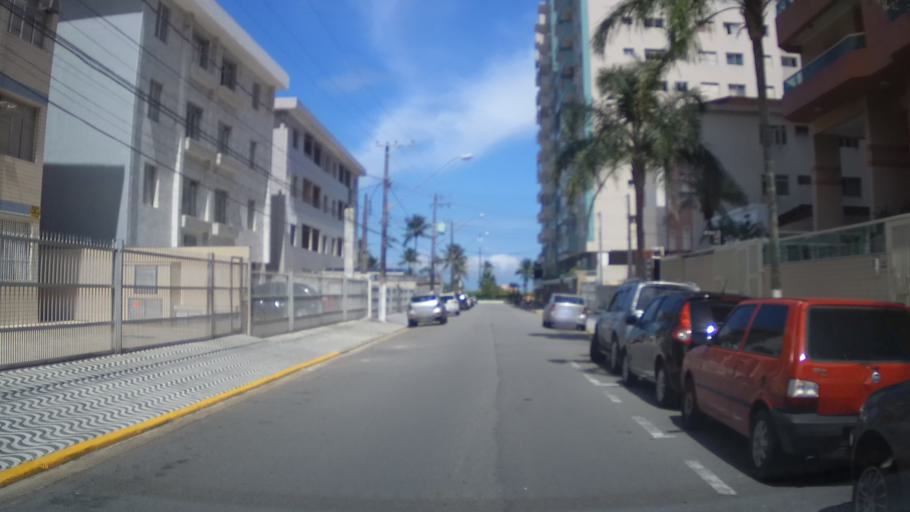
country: BR
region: Sao Paulo
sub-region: Praia Grande
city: Praia Grande
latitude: -24.0145
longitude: -46.4019
